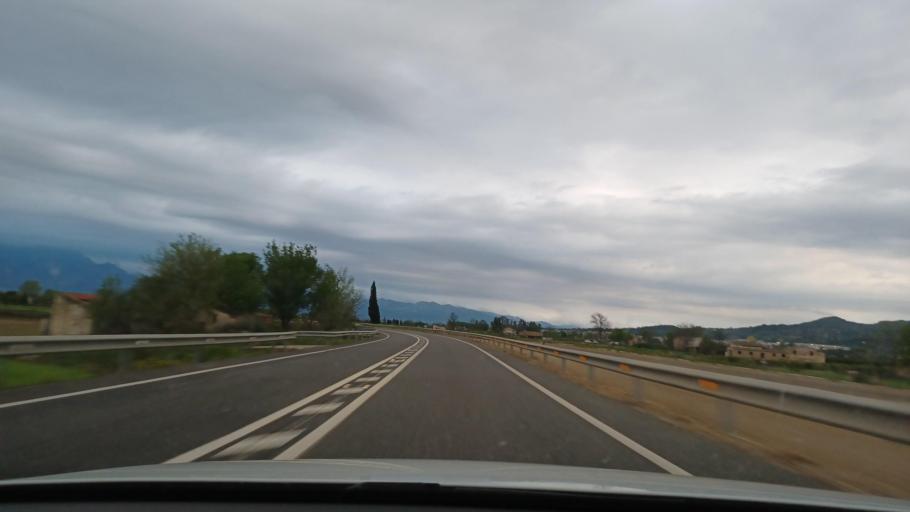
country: ES
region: Catalonia
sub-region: Provincia de Tarragona
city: Amposta
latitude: 40.7454
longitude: 0.5606
